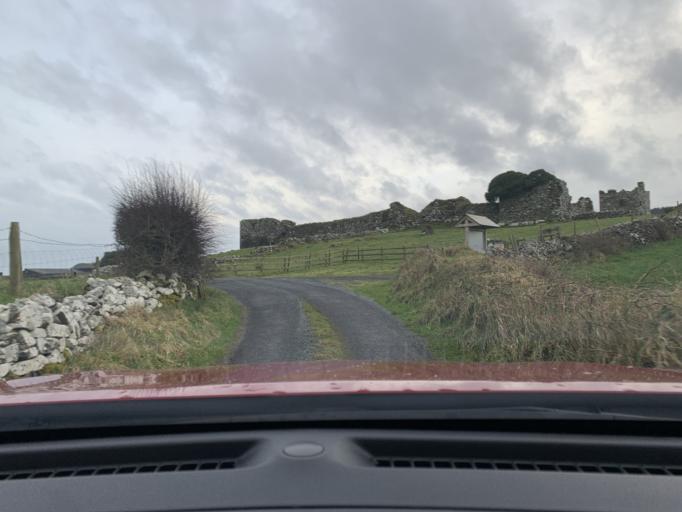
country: IE
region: Connaught
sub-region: Sligo
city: Ballymote
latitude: 53.9726
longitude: -8.4750
